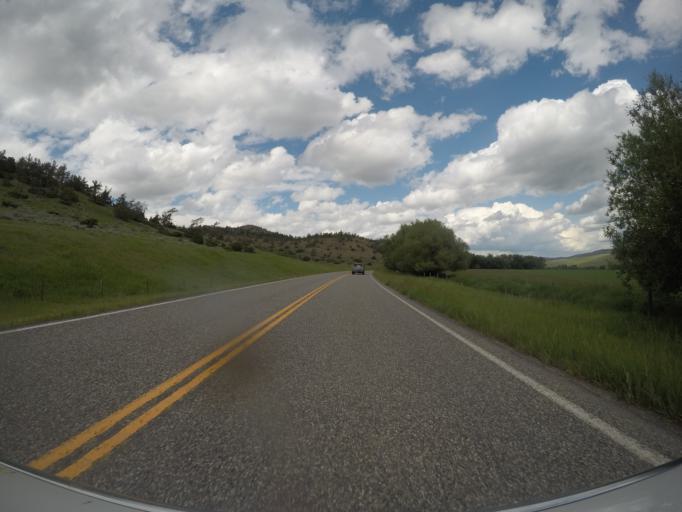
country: US
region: Montana
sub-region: Sweet Grass County
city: Big Timber
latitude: 45.6834
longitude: -110.0840
